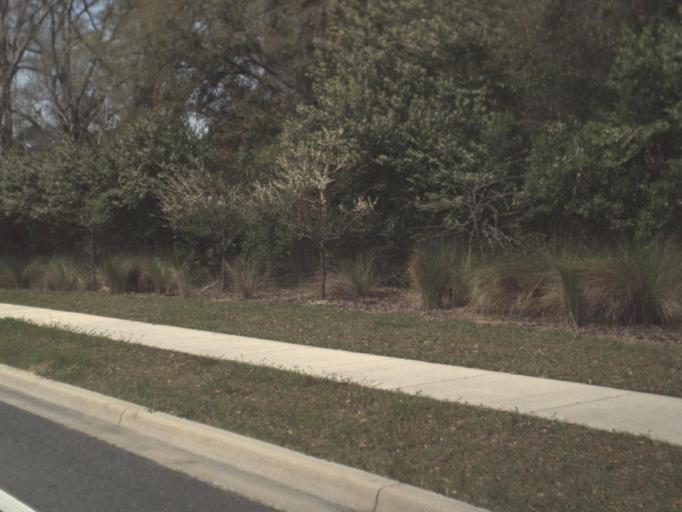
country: US
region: Florida
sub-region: Leon County
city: Tallahassee
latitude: 30.3759
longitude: -84.2675
